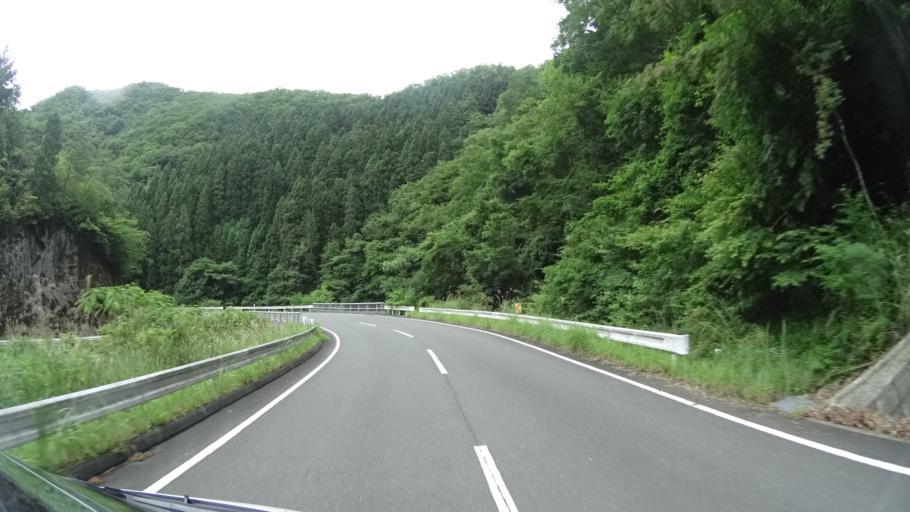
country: JP
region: Hyogo
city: Sasayama
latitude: 35.0631
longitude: 135.3944
